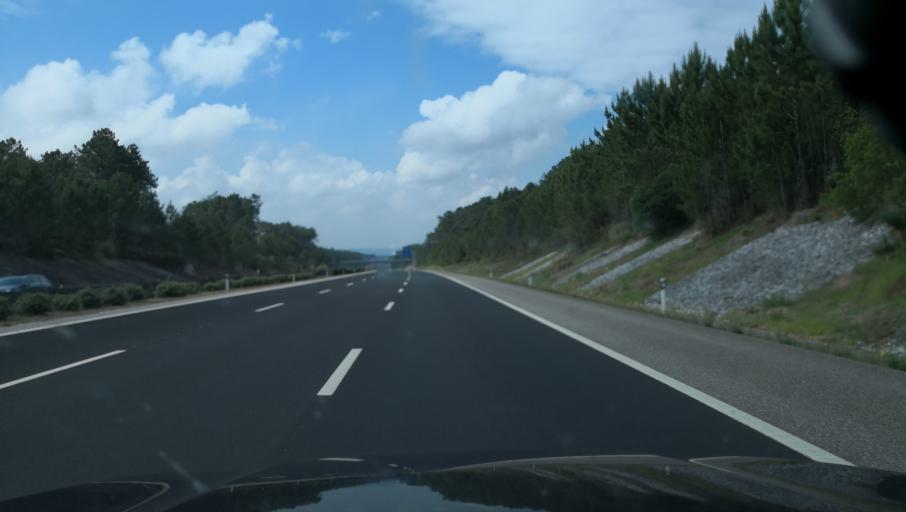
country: PT
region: Leiria
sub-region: Alcobaca
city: Pataias
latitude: 39.6609
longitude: -8.9582
